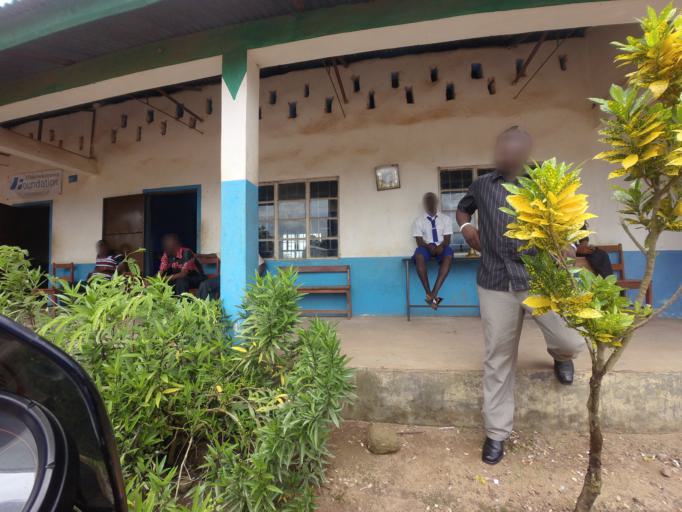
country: SL
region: Northern Province
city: Kambia
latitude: 9.1039
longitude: -12.9238
